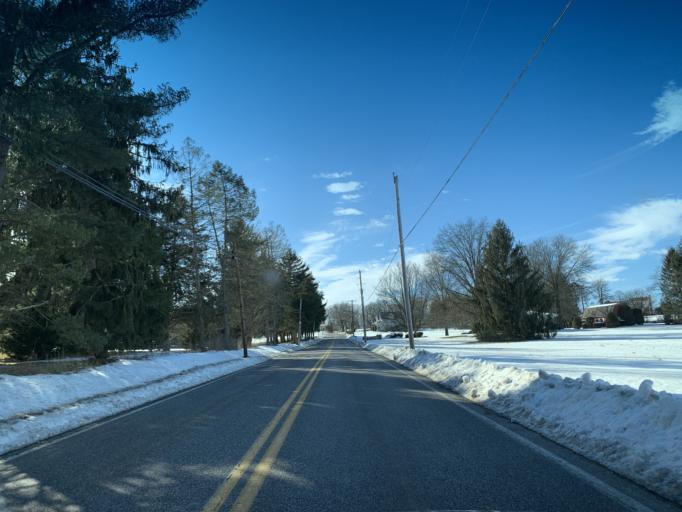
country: US
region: Pennsylvania
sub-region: York County
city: Dillsburg
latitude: 40.0529
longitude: -76.9499
